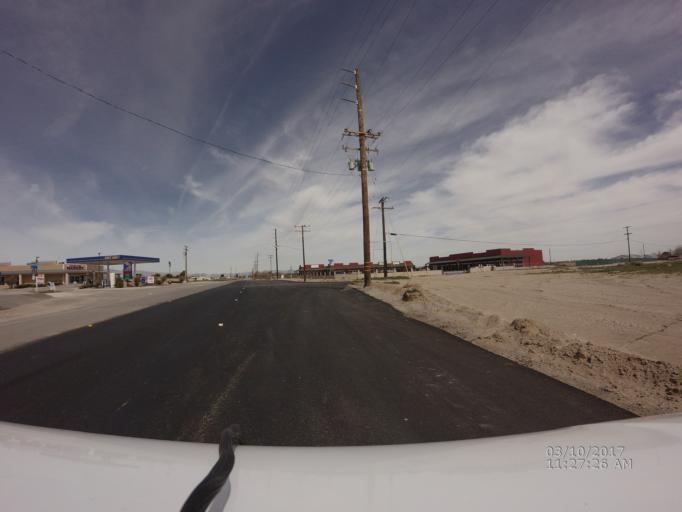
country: US
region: California
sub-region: Los Angeles County
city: Quartz Hill
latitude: 34.7543
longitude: -118.2899
